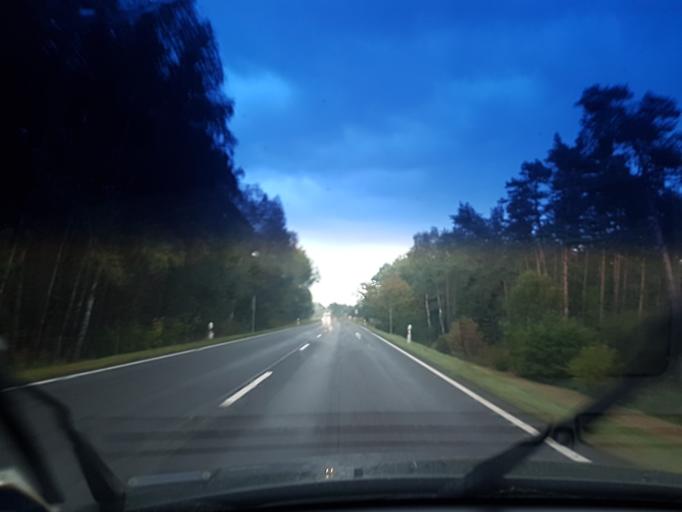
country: DE
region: Bavaria
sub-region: Upper Franconia
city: Frensdorf
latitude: 49.7771
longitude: 10.9019
